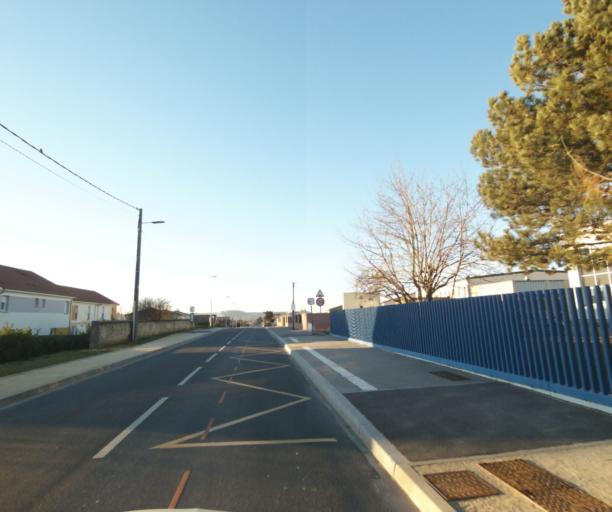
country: FR
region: Lorraine
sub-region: Departement de Meurthe-et-Moselle
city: Tomblaine
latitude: 48.6743
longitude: 6.2239
